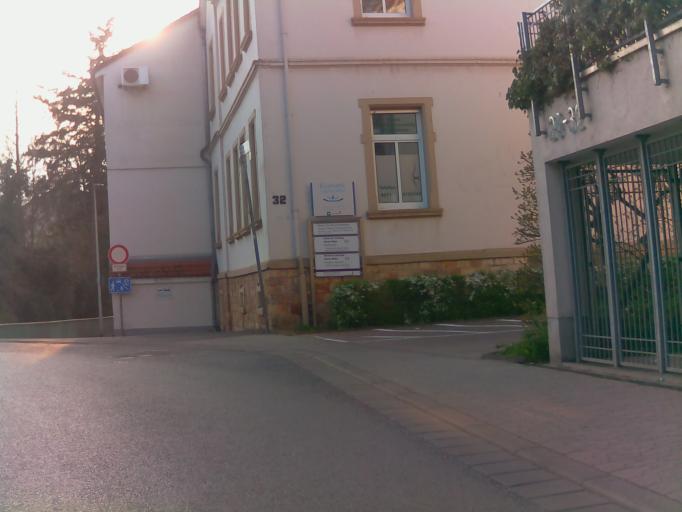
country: DE
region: Rheinland-Pfalz
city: Bad Kreuznach
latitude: 49.8478
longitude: 7.8498
